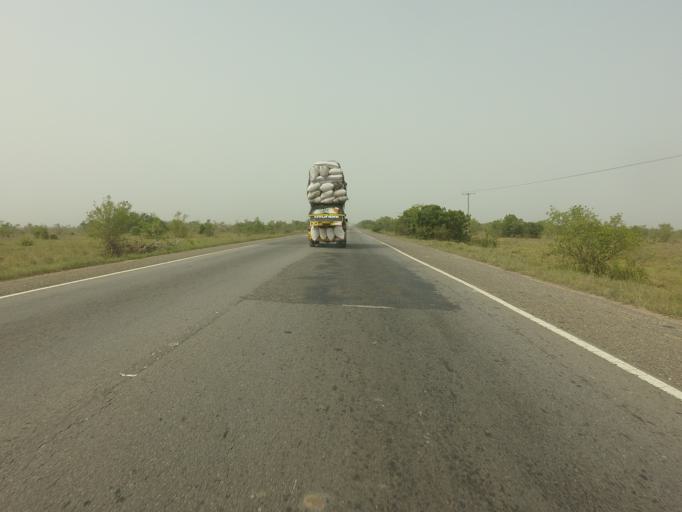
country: GH
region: Volta
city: Anloga
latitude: 5.9631
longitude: 0.5244
